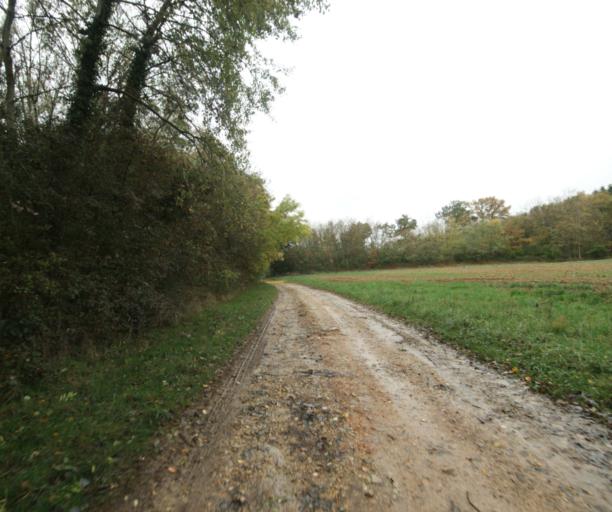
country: FR
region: Bourgogne
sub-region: Departement de Saone-et-Loire
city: Saint-Martin-Belle-Roche
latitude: 46.4785
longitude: 4.8496
